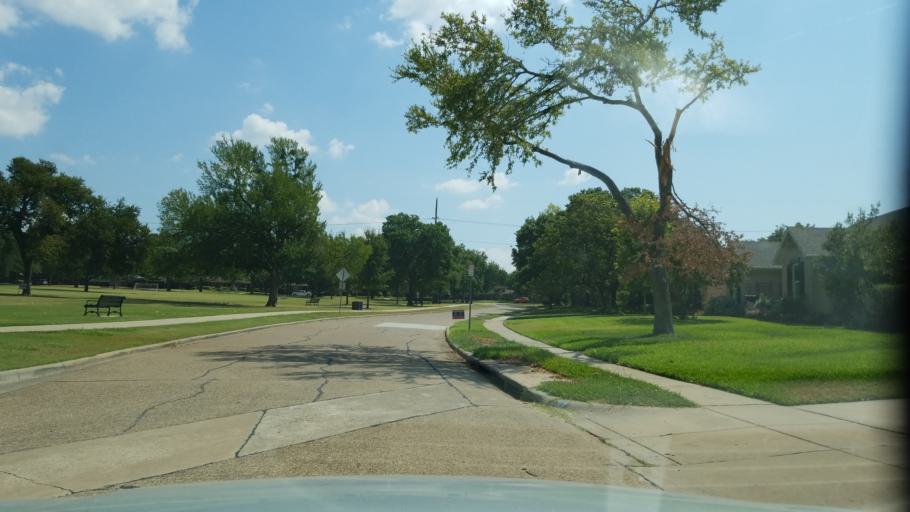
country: US
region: Texas
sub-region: Dallas County
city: Richardson
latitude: 32.9588
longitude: -96.7460
